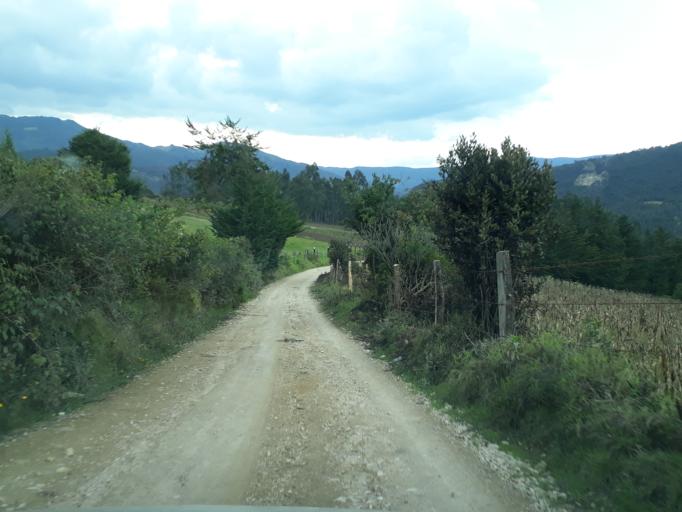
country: CO
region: Cundinamarca
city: Lenguazaque
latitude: 5.2607
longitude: -73.6916
